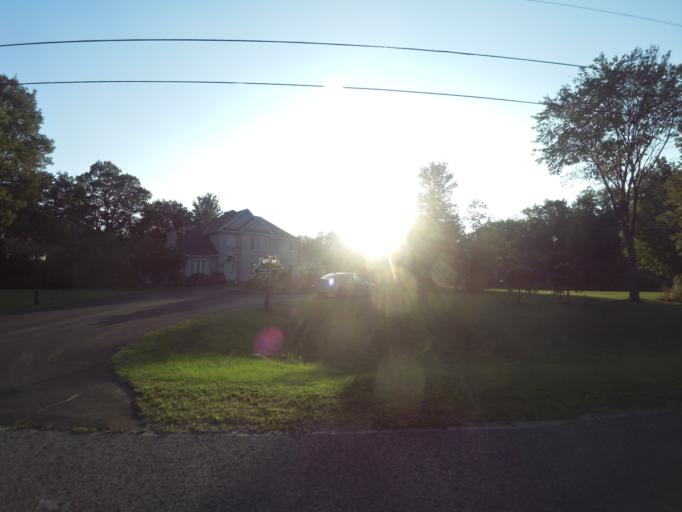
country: CA
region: Ontario
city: Clarence-Rockland
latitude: 45.5049
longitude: -75.4309
